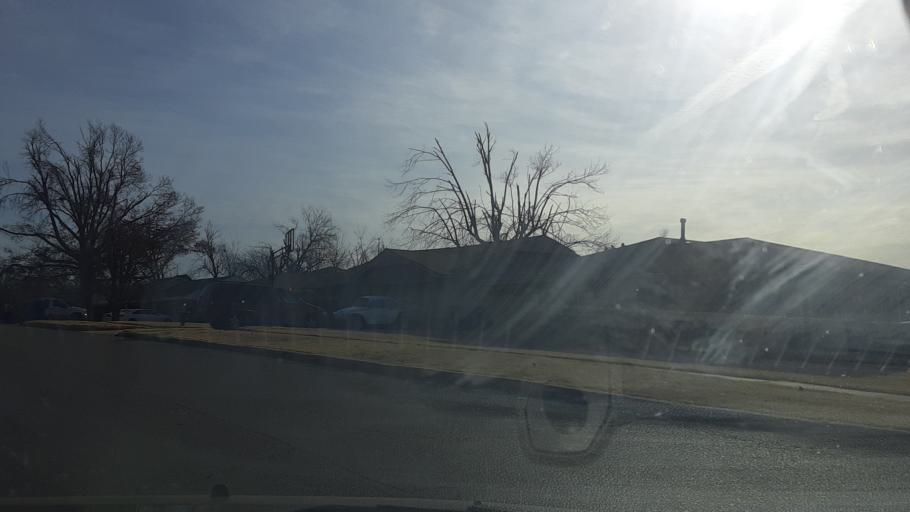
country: US
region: Oklahoma
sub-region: Logan County
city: Guthrie
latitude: 35.8911
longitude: -97.4163
